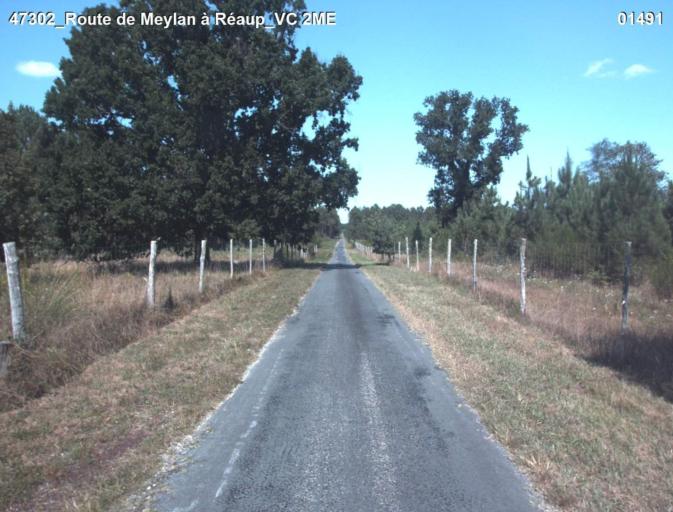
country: FR
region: Aquitaine
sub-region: Departement du Lot-et-Garonne
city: Mezin
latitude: 44.0958
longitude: 0.1323
